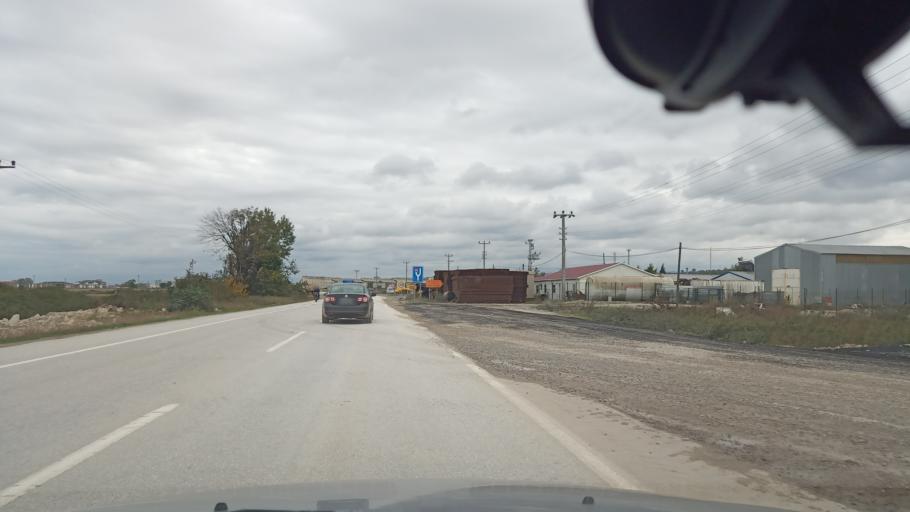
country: TR
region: Sakarya
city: Karasu
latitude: 41.1140
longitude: 30.6560
